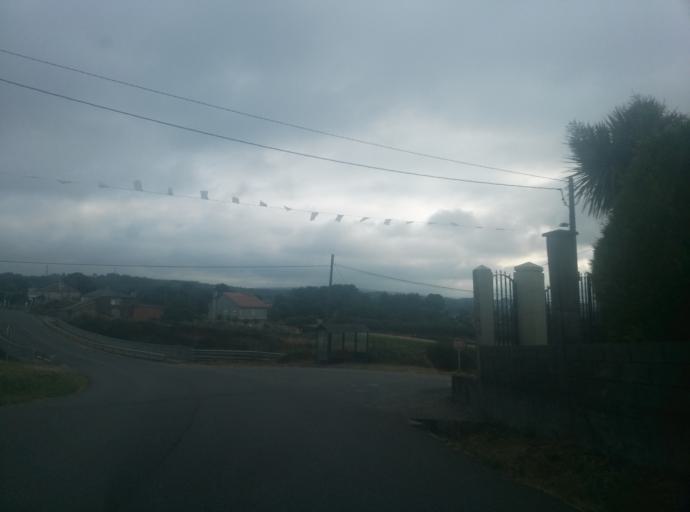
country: ES
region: Galicia
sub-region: Provincia de Lugo
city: Lugo
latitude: 43.0621
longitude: -7.5655
